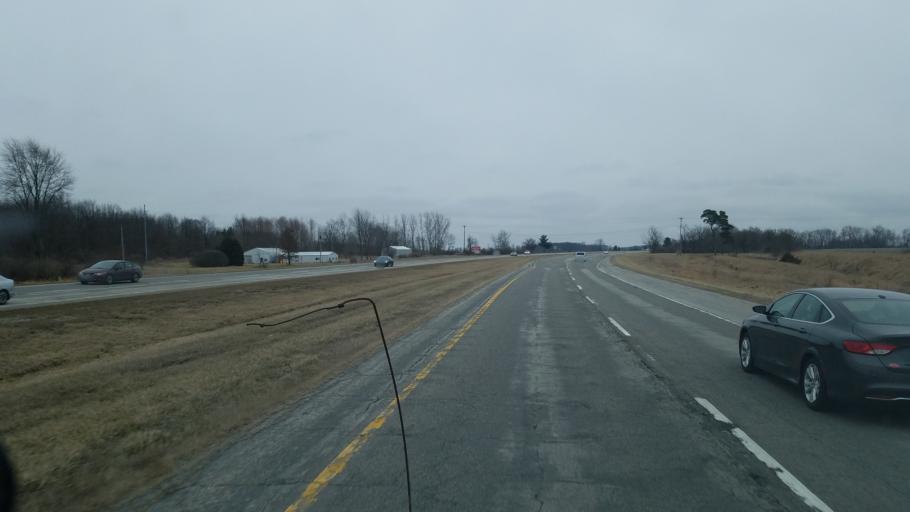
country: US
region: Indiana
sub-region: Fulton County
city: Rochester
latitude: 41.0129
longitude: -86.1697
